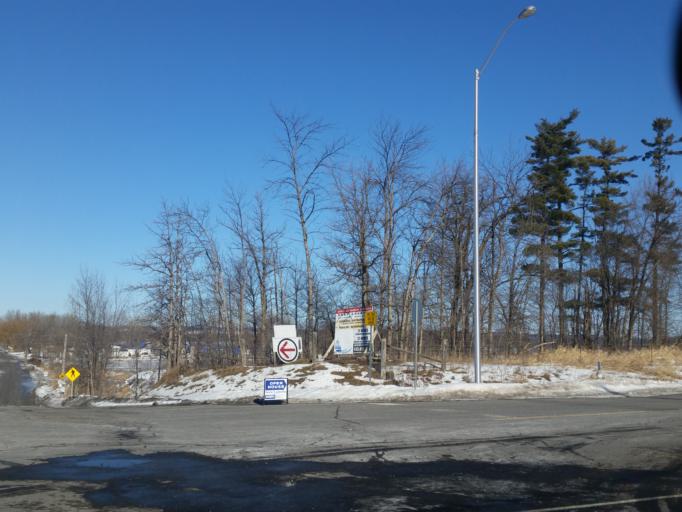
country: CA
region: Ontario
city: Clarence-Rockland
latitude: 45.4971
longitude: -75.4831
